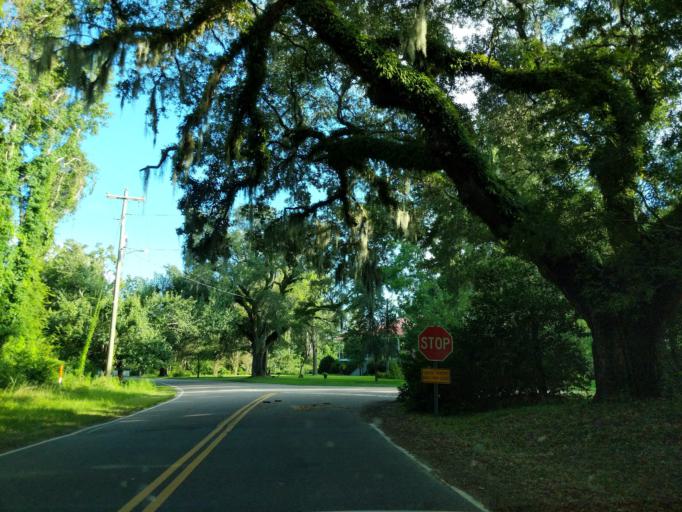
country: US
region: South Carolina
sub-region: Charleston County
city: Awendaw
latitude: 33.0932
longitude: -79.4652
